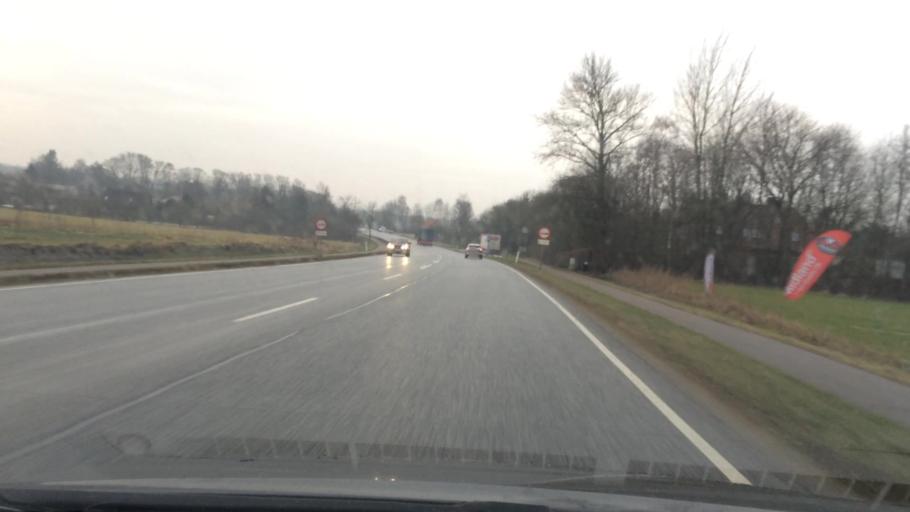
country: DK
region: Central Jutland
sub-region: Horsens Kommune
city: Horsens
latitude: 55.8235
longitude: 9.7935
